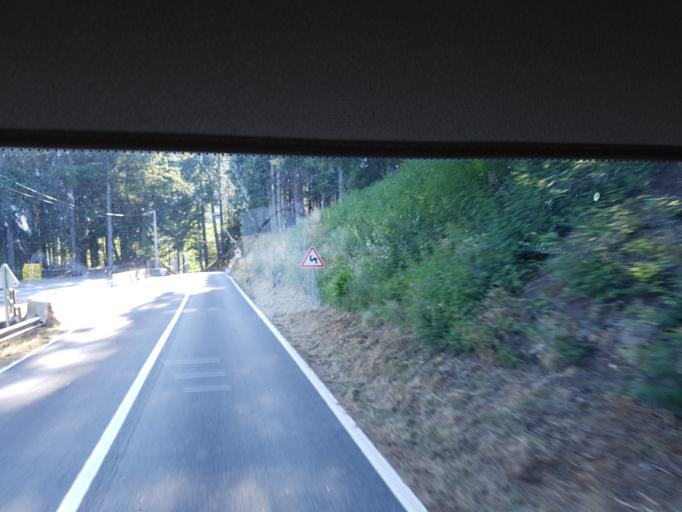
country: PT
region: Castelo Branco
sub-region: Covilha
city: Covilha
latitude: 40.2820
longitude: -7.5234
